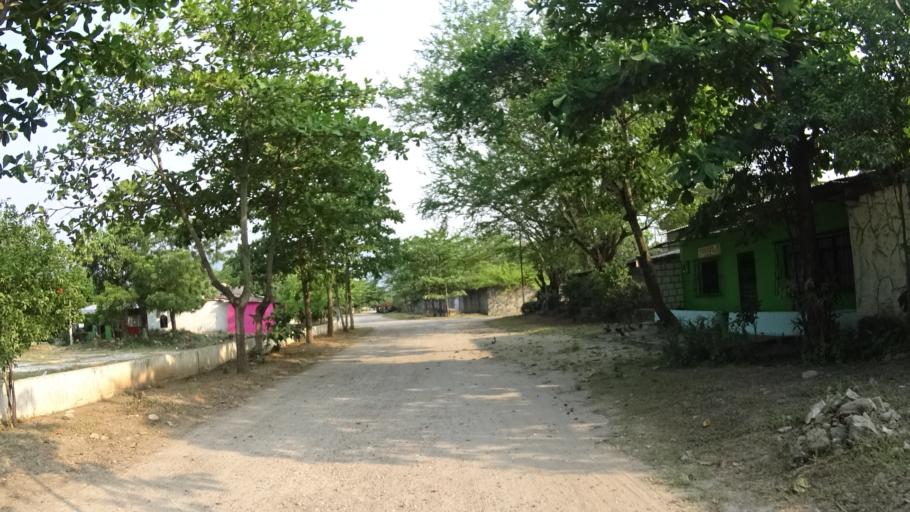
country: CO
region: Caldas
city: La Dorada
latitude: 5.4574
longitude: -74.6630
